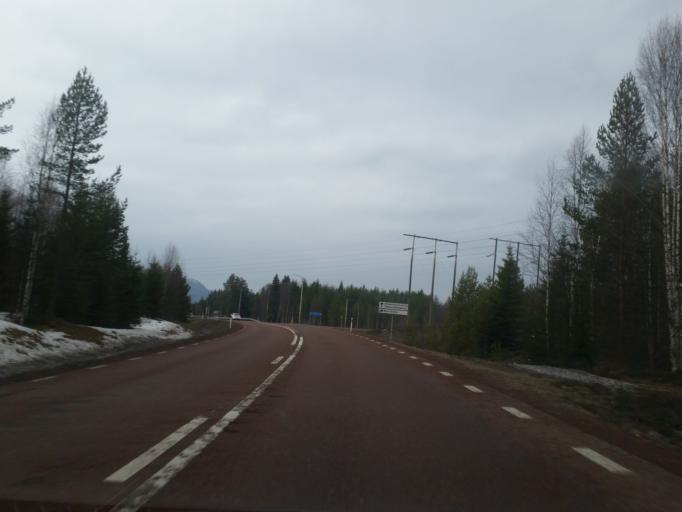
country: SE
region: Dalarna
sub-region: Alvdalens Kommun
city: AElvdalen
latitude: 61.1457
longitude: 14.1543
